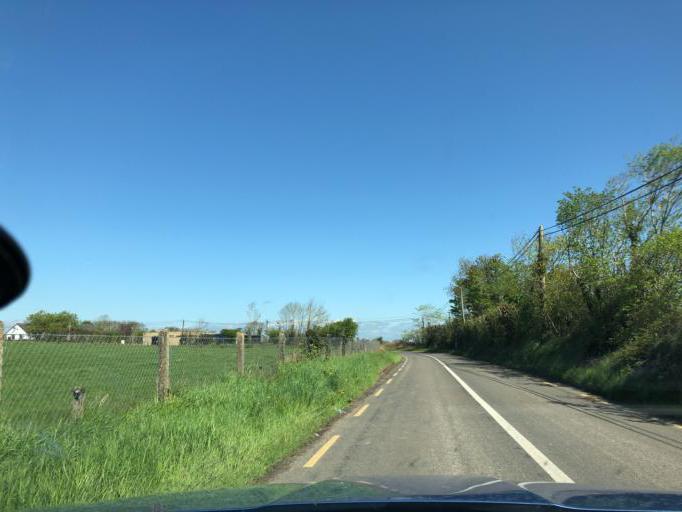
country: IE
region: Connaught
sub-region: County Galway
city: Portumna
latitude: 53.1311
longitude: -8.3537
